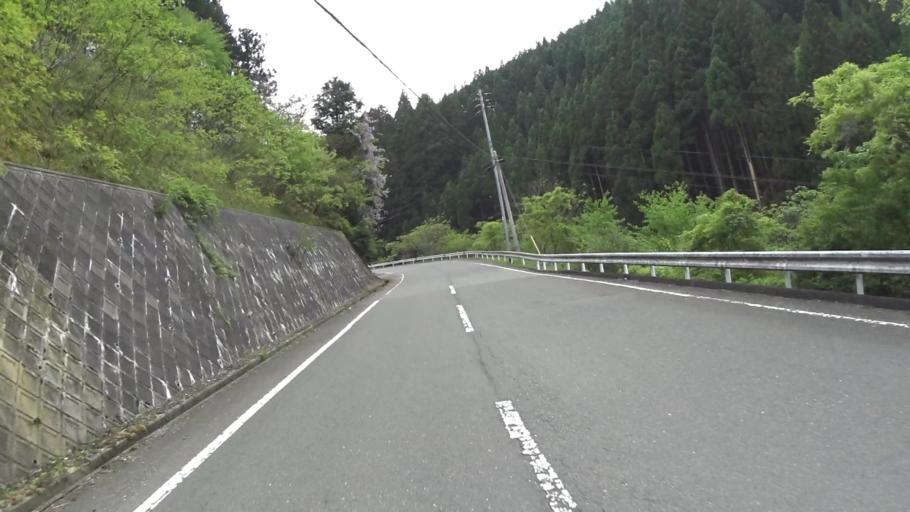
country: JP
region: Kyoto
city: Kameoka
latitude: 35.1321
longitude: 135.6195
